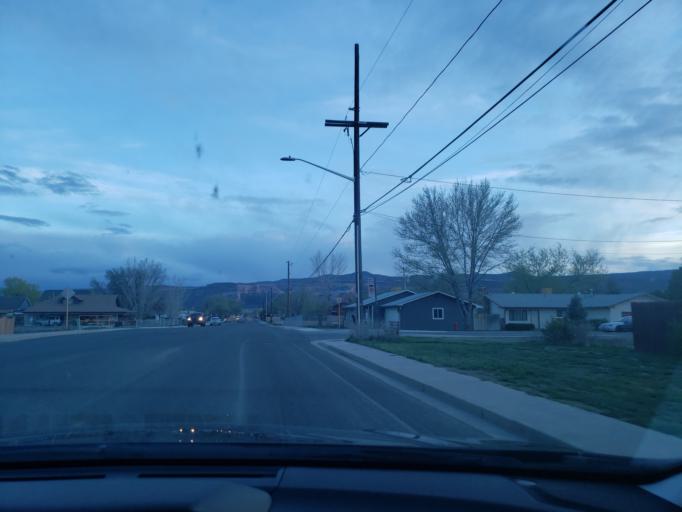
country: US
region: Colorado
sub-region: Mesa County
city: Fruita
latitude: 39.1567
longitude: -108.7198
